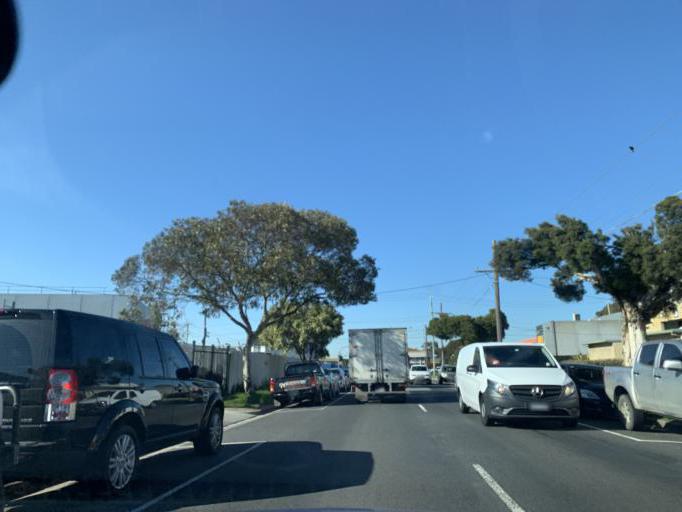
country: AU
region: Victoria
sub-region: Greater Dandenong
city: Keysborough
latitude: -37.9922
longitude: 145.1883
